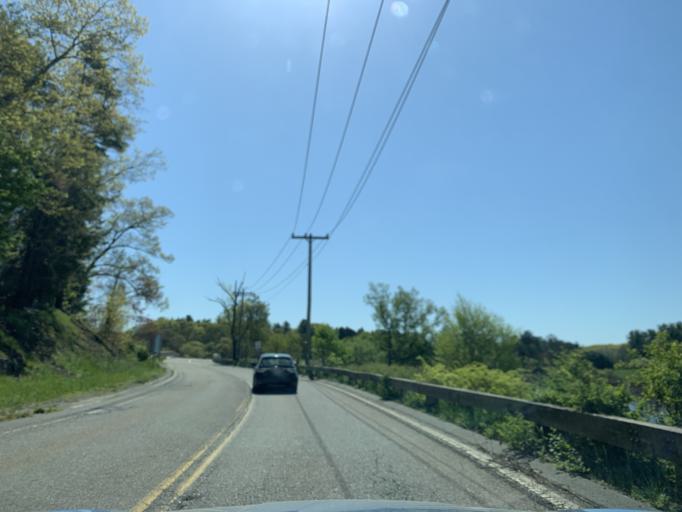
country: US
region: Massachusetts
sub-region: Middlesex County
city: Concord
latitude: 42.4204
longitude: -71.3662
